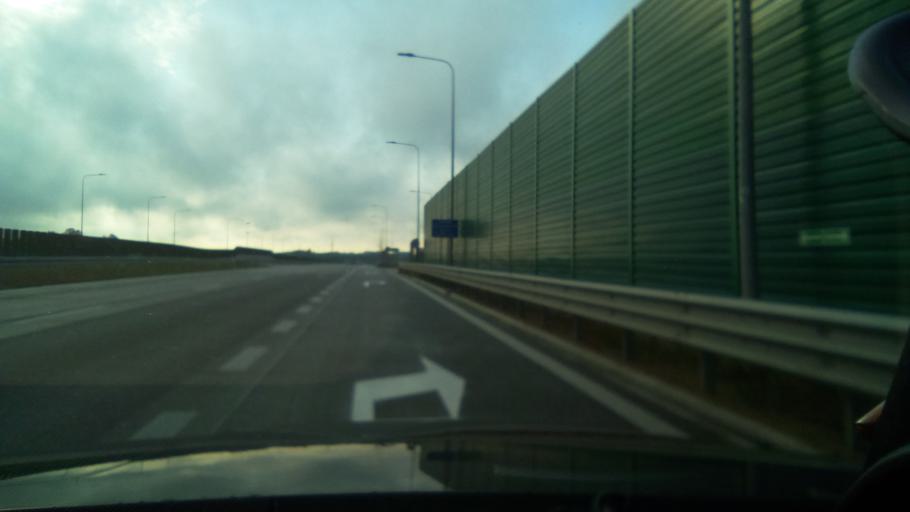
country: PL
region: Silesian Voivodeship
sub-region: Powiat czestochowski
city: Konopiska
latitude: 50.7458
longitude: 19.0419
